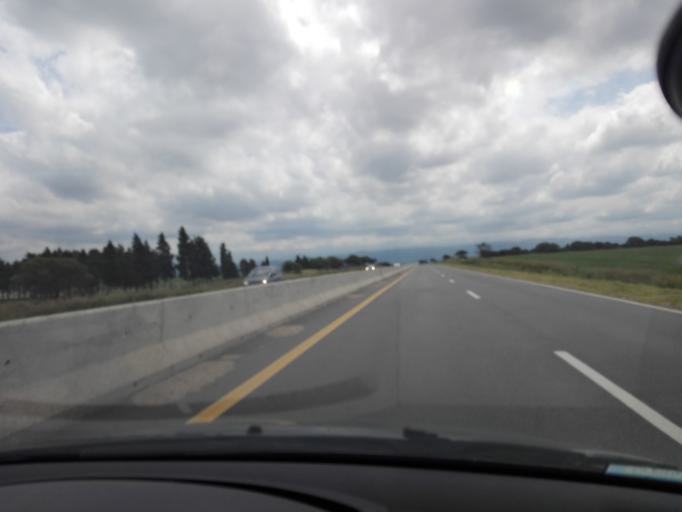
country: AR
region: Cordoba
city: Alta Gracia
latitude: -31.6521
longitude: -64.3221
